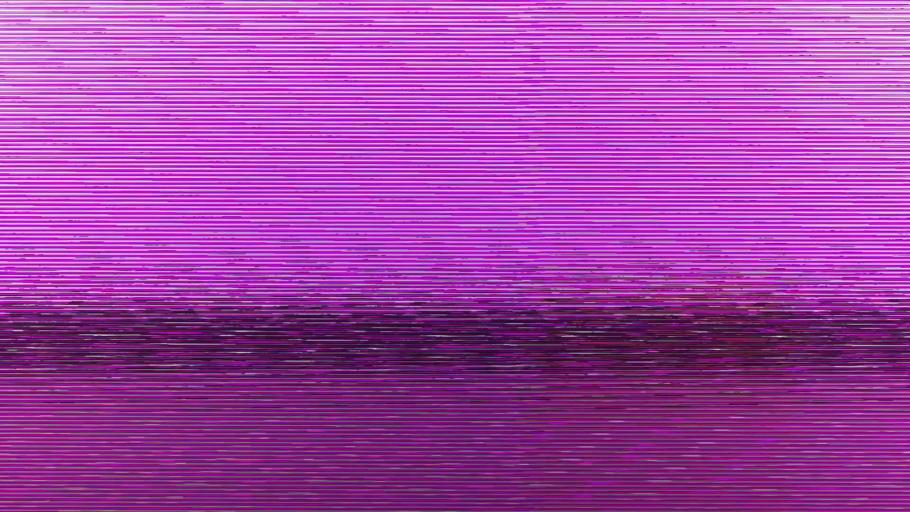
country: US
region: Michigan
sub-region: Wayne County
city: Belleville
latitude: 42.2213
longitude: -83.4852
